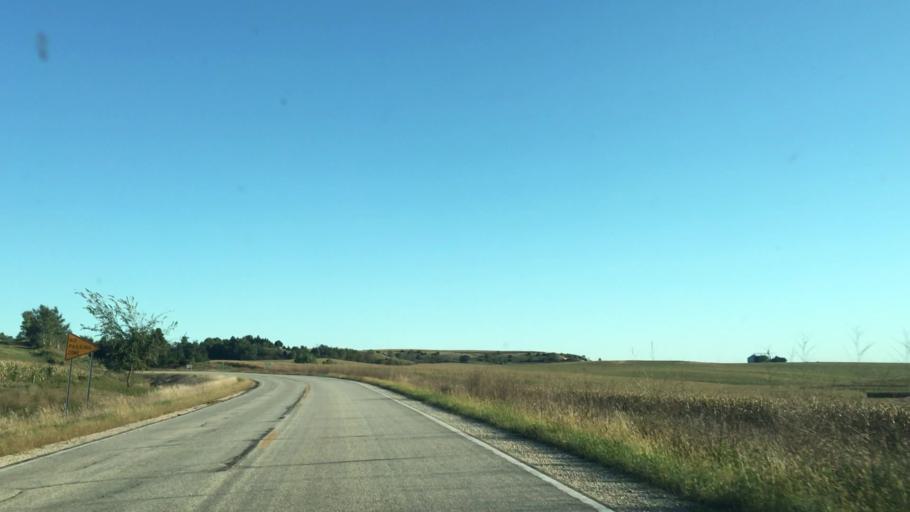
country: US
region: Minnesota
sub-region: Fillmore County
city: Chatfield
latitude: 43.8486
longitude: -92.1063
